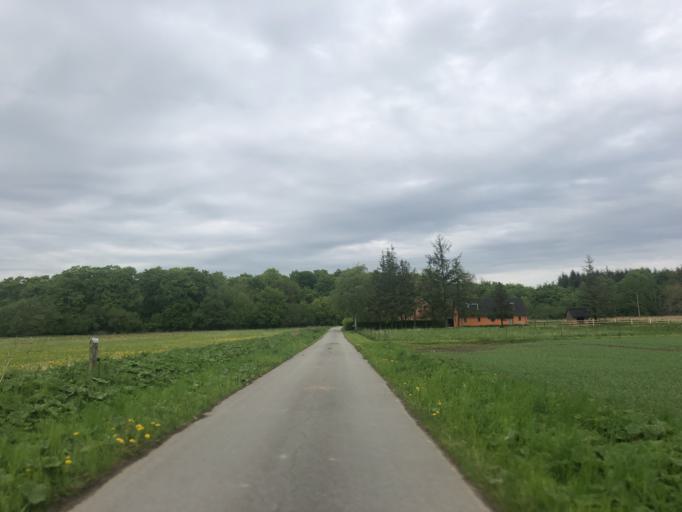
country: DK
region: Zealand
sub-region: Koge Kommune
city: Bjaeverskov
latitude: 55.4307
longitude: 12.0810
